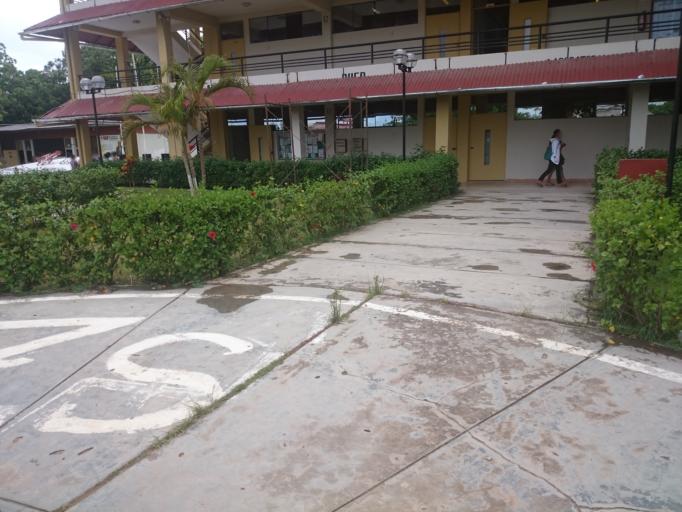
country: PE
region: Ucayali
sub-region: Provincia de Coronel Portillo
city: Puerto Callao
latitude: -8.3709
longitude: -74.5676
